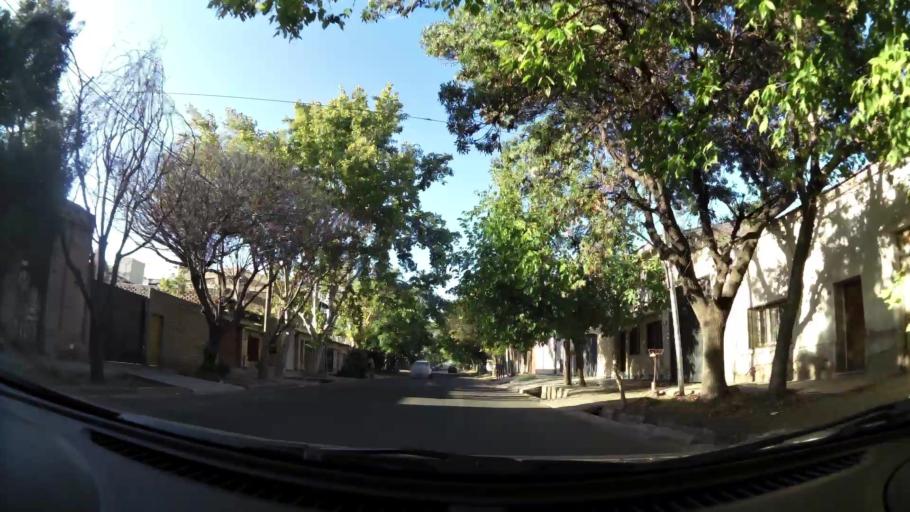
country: AR
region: Mendoza
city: Las Heras
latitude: -32.8645
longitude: -68.8259
